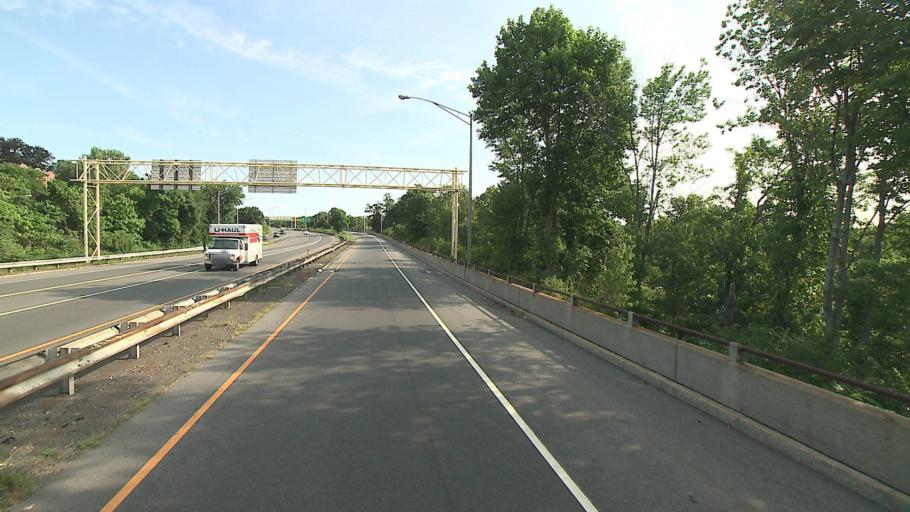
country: US
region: Connecticut
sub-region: Fairfield County
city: Norwalk
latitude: 41.1076
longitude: -73.4196
